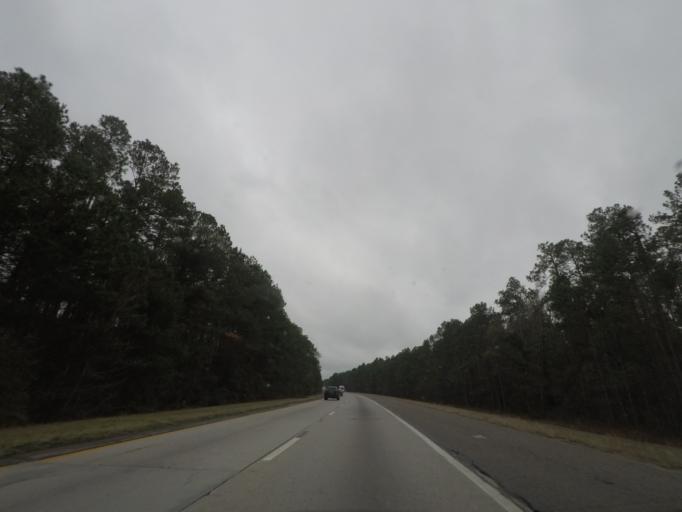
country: US
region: South Carolina
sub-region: Colleton County
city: Walterboro
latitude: 33.0434
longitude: -80.6700
